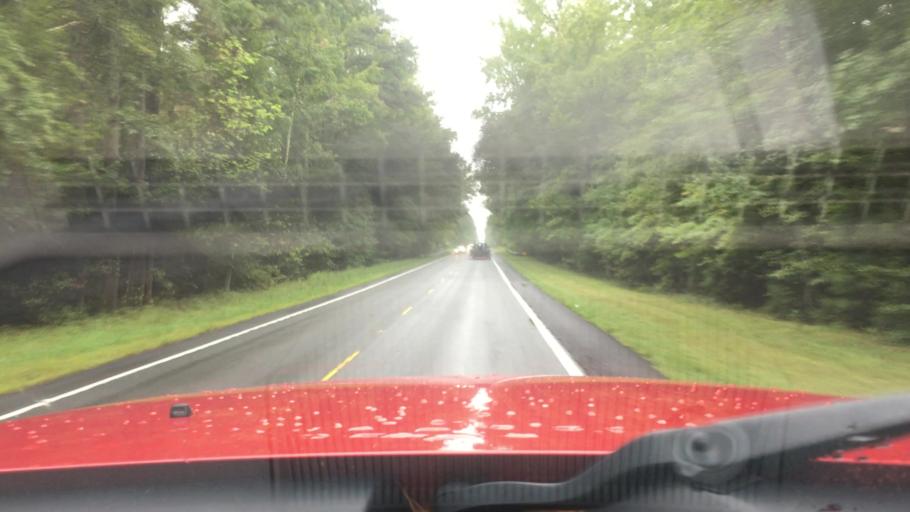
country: US
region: Virginia
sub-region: Caroline County
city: Bowling Green
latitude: 37.9621
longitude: -77.3431
